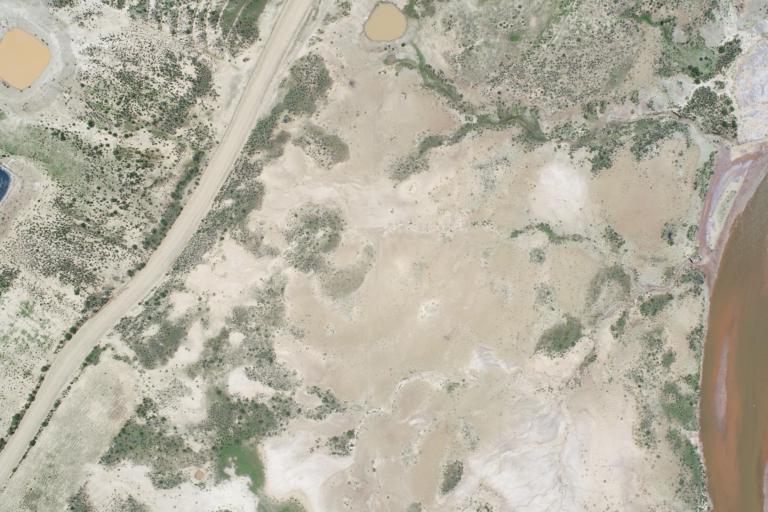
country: BO
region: La Paz
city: Curahuara de Carangas
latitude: -17.3072
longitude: -68.4950
